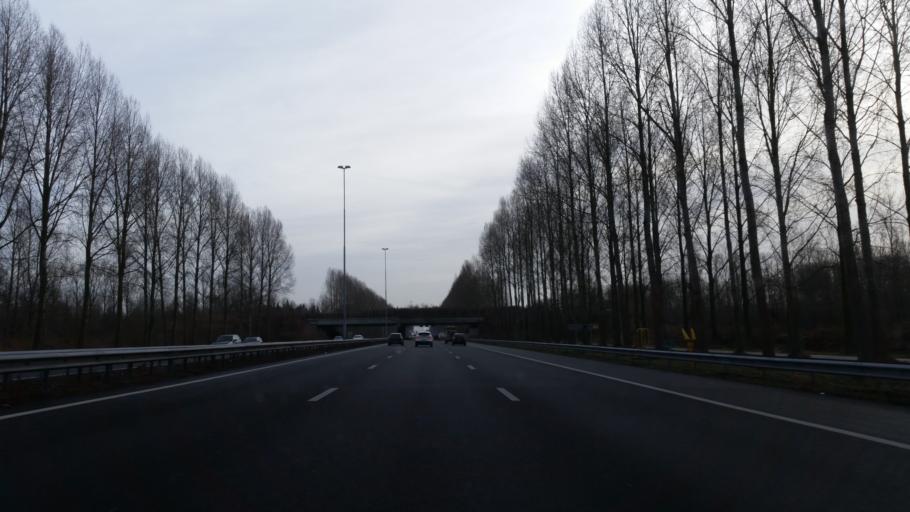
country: NL
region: North Brabant
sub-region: Gemeente Best
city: Best
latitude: 51.5412
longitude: 5.3750
